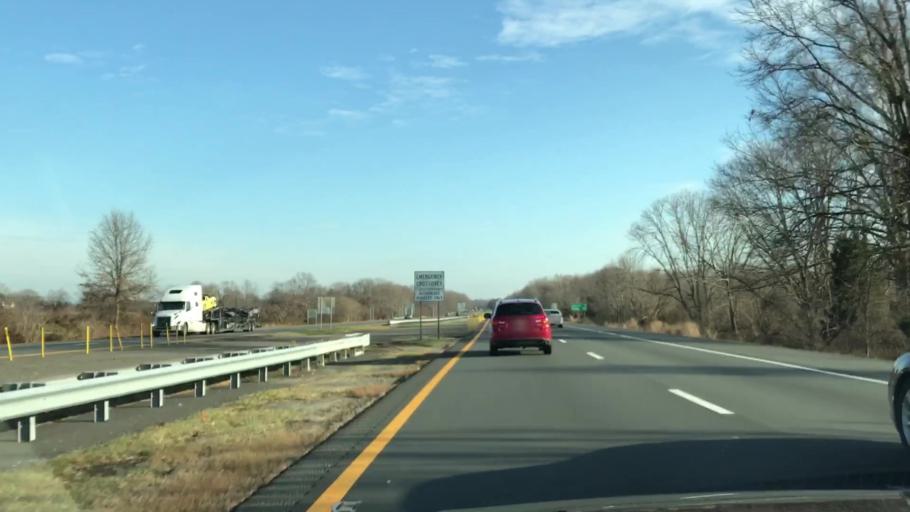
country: US
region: New Jersey
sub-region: Monmouth County
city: Allentown
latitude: 40.1830
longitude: -74.5621
